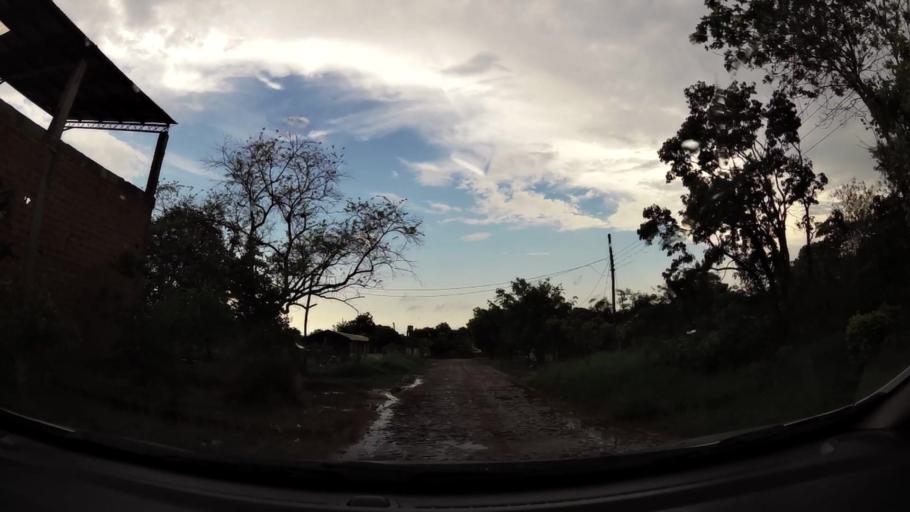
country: PY
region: Alto Parana
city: Presidente Franco
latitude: -25.5408
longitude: -54.6534
